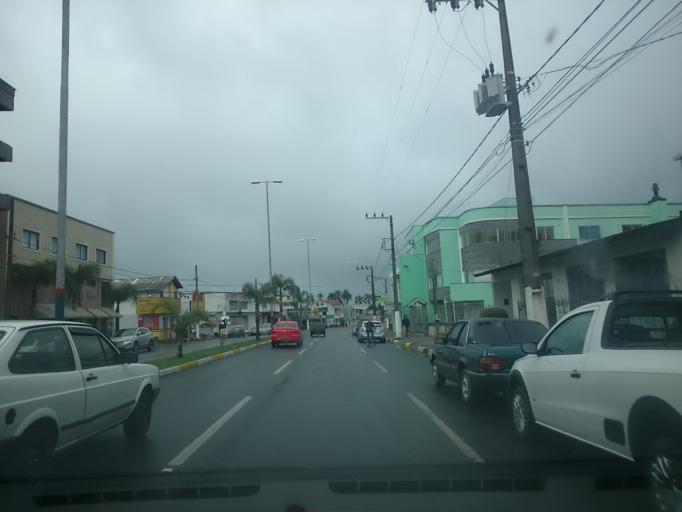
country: BR
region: Santa Catarina
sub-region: Lages
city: Lages
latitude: -27.8251
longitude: -50.3347
